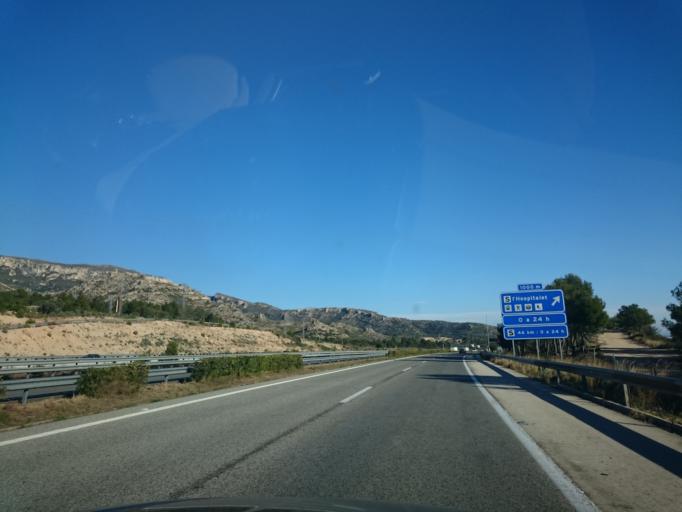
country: ES
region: Catalonia
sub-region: Provincia de Tarragona
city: l'Ametlla de Mar
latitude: 40.9770
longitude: 0.8819
